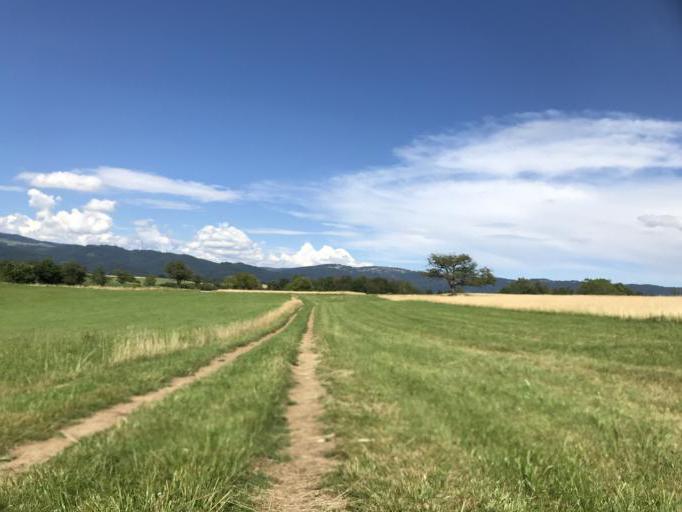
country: DE
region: Baden-Wuerttemberg
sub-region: Freiburg Region
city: Schopfheim
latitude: 47.6338
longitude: 7.8407
